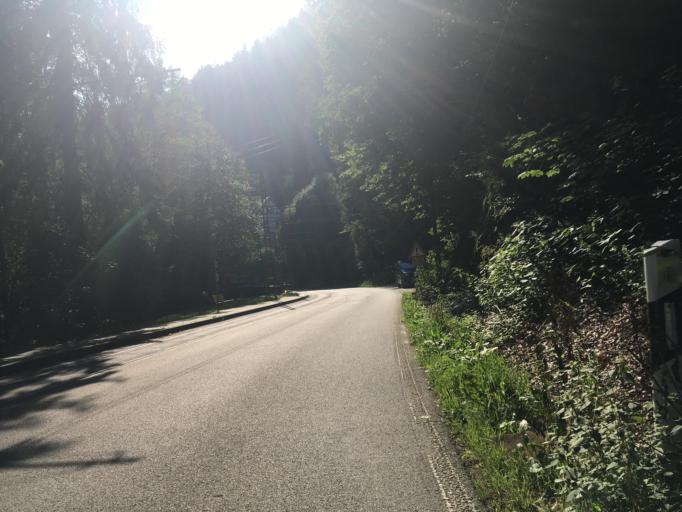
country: DE
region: Saxony
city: Bad Schandau
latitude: 50.9303
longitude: 14.1913
